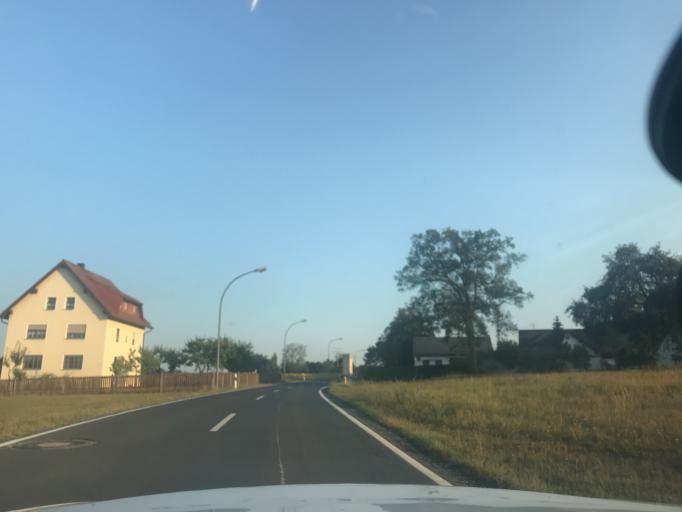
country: DE
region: Bavaria
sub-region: Upper Franconia
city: Pegnitz
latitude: 49.7085
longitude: 11.5774
